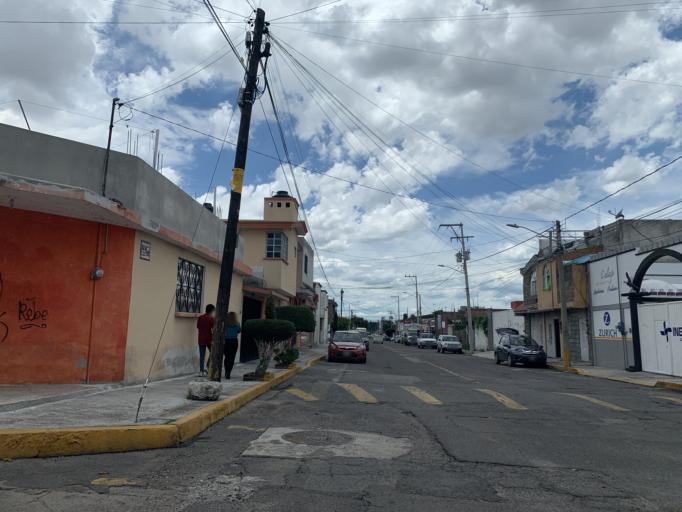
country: MX
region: Puebla
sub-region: Cuautlancingo
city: Sanctorum
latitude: 19.0751
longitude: -98.2359
